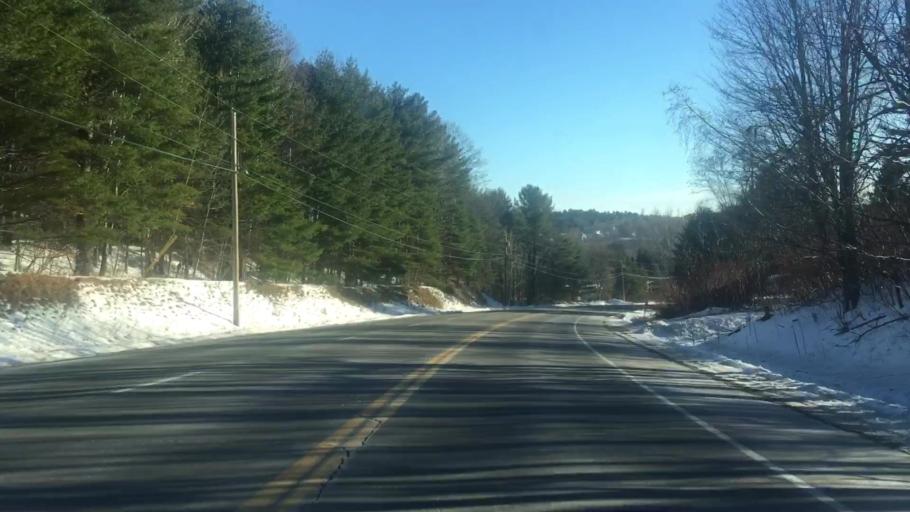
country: US
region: Maine
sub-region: Somerset County
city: Norridgewock
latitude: 44.7210
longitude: -69.7986
